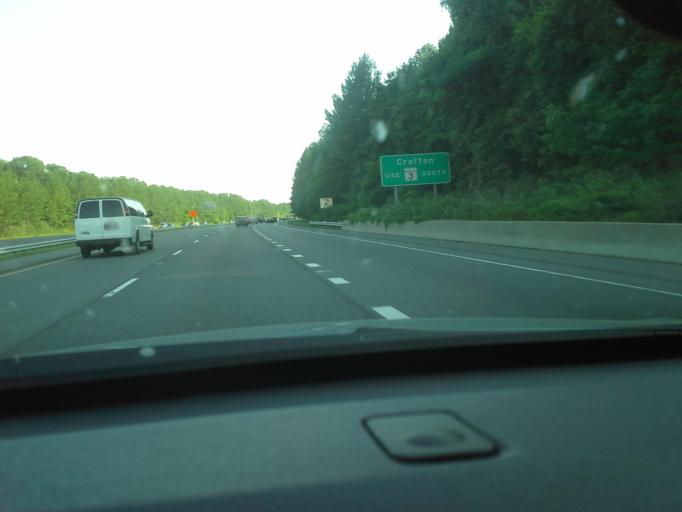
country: US
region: Maryland
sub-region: Anne Arundel County
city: Gambrills
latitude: 39.0789
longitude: -76.6280
